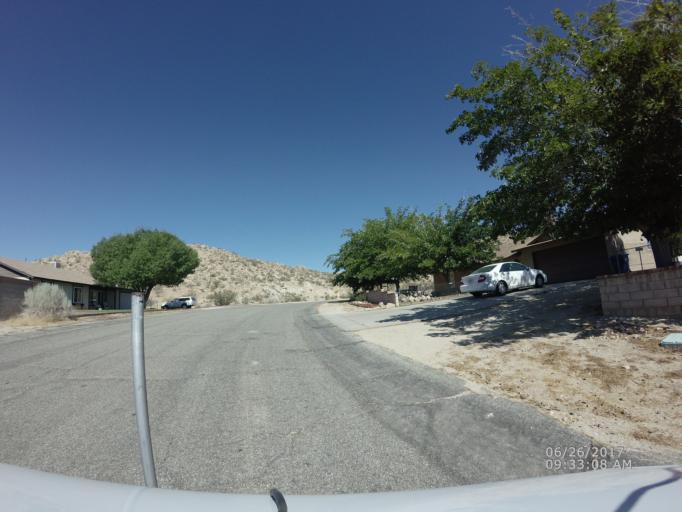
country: US
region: California
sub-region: Los Angeles County
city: Lake Los Angeles
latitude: 34.6026
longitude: -117.8131
